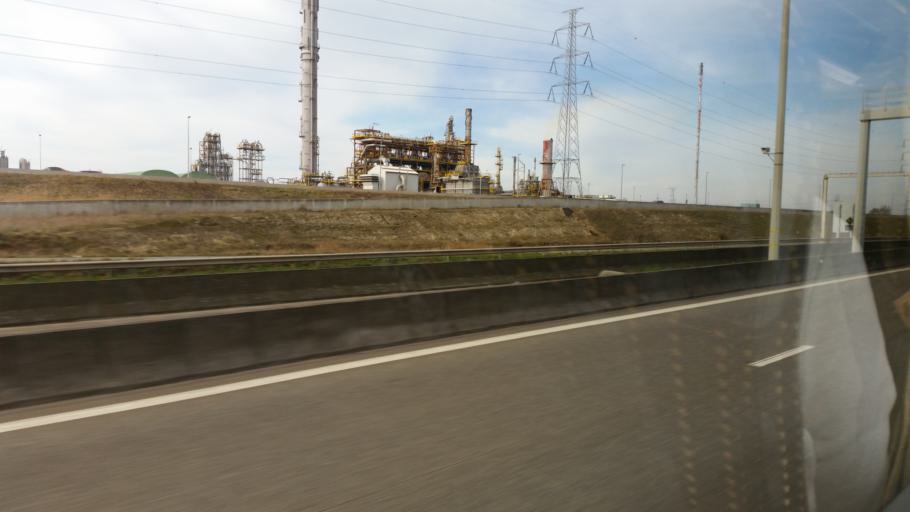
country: BE
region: Flanders
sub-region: Provincie Oost-Vlaanderen
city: Beveren
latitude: 51.2699
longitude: 4.2768
